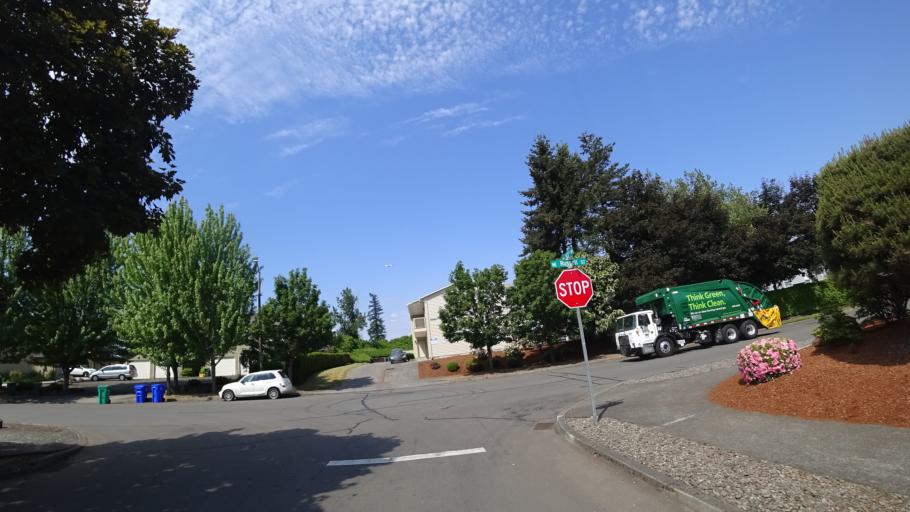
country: US
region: Oregon
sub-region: Multnomah County
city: Fairview
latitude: 45.5414
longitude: -122.4924
